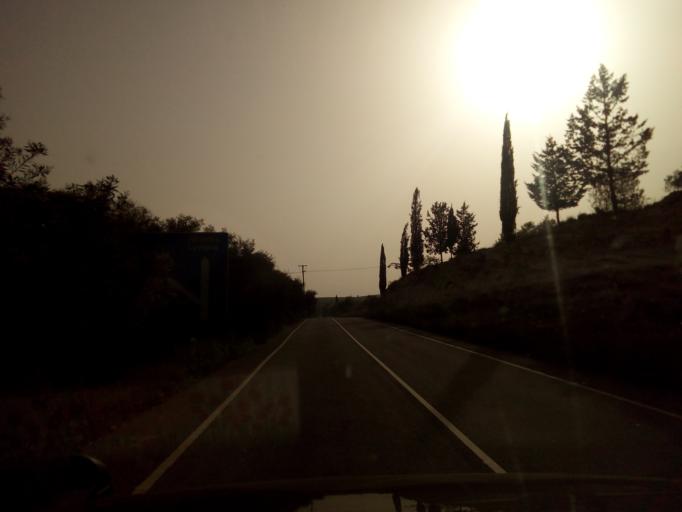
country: CY
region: Lefkosia
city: Lympia
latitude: 34.9982
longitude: 33.4889
